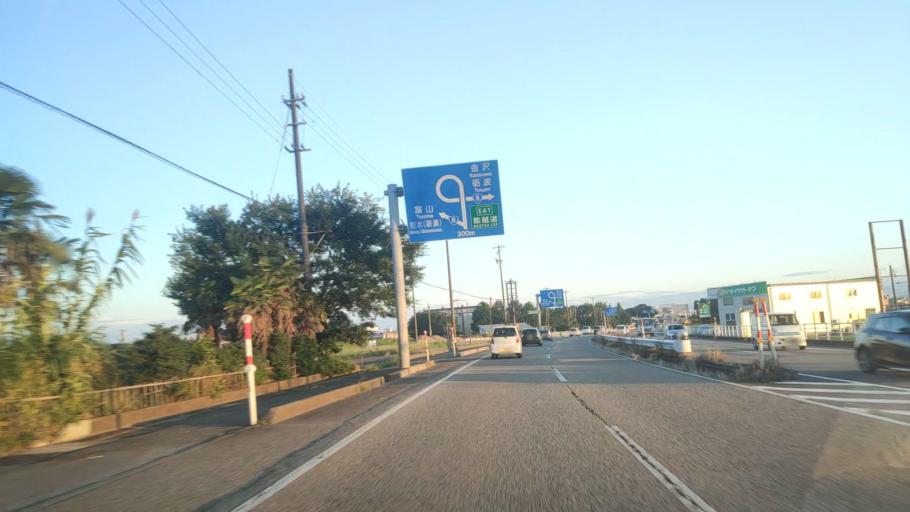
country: JP
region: Toyama
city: Takaoka
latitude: 36.7666
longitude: 137.0052
